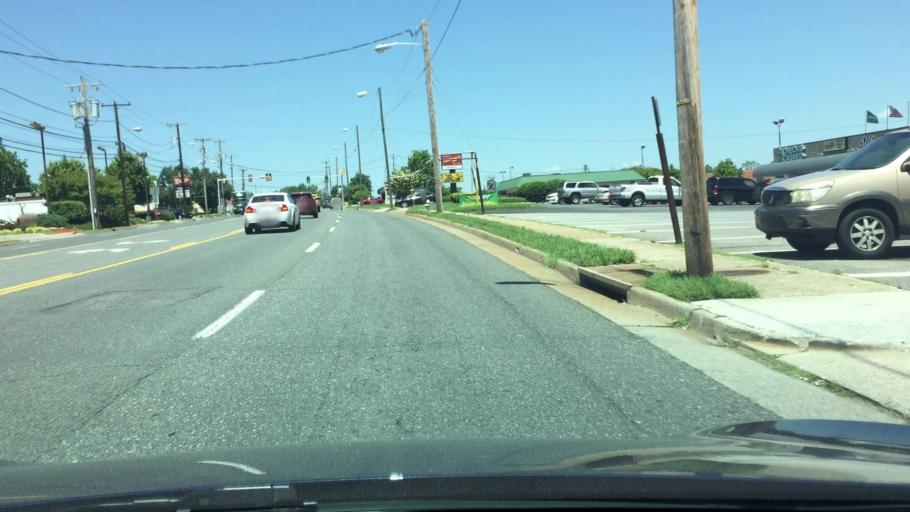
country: US
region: Virginia
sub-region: City of Lynchburg
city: West Lynchburg
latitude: 37.3720
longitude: -79.1840
